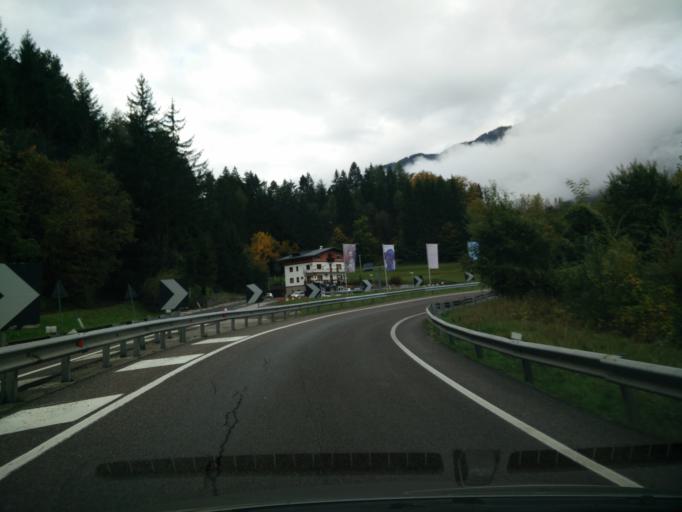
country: IT
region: Veneto
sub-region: Provincia di Belluno
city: Pieve di Cadore
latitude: 46.4200
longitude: 12.3682
